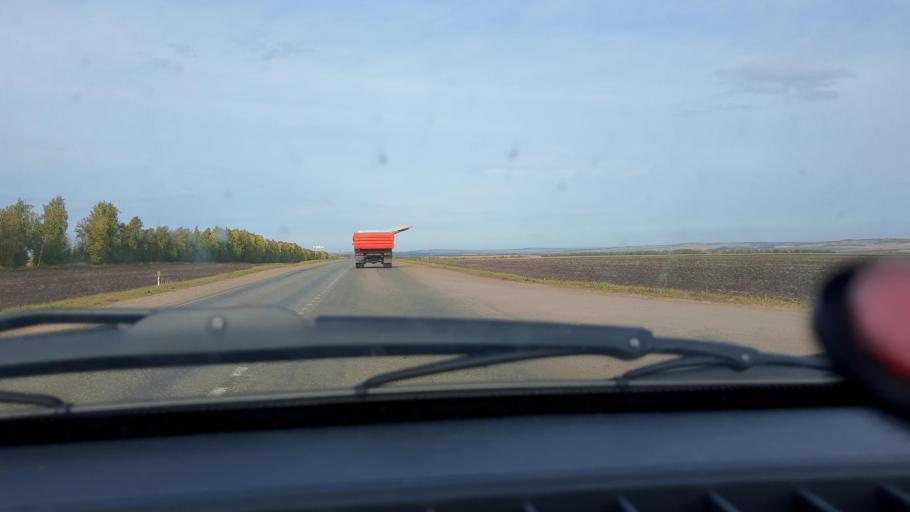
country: RU
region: Bashkortostan
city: Chekmagush
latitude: 55.0042
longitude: 54.5854
